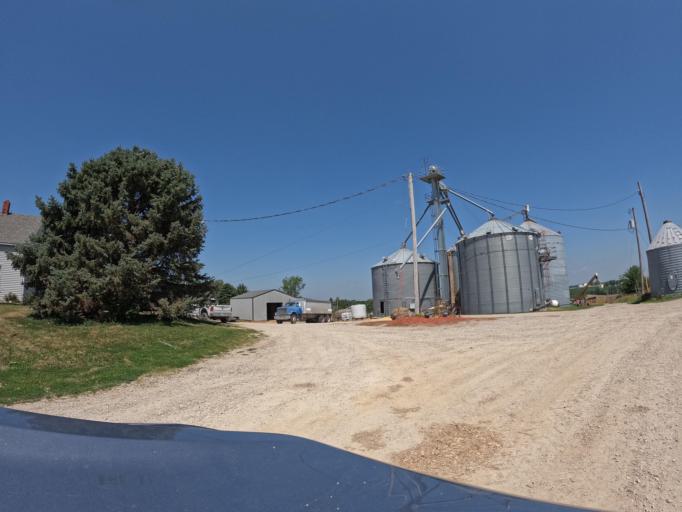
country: US
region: Iowa
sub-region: Keokuk County
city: Sigourney
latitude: 41.2703
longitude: -92.2190
